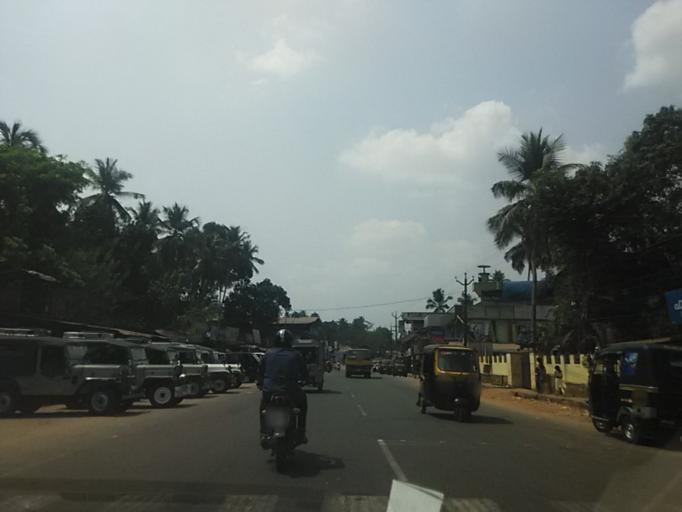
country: IN
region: Kerala
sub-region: Kozhikode
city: Naduvannur
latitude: 11.4883
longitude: 75.7749
